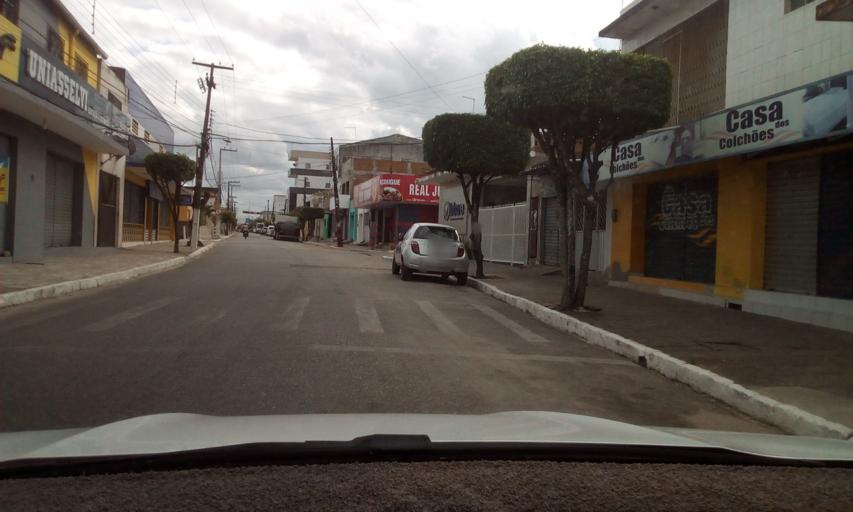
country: BR
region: Paraiba
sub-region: Mamanguape
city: Mamanguape
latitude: -6.8357
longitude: -35.1257
